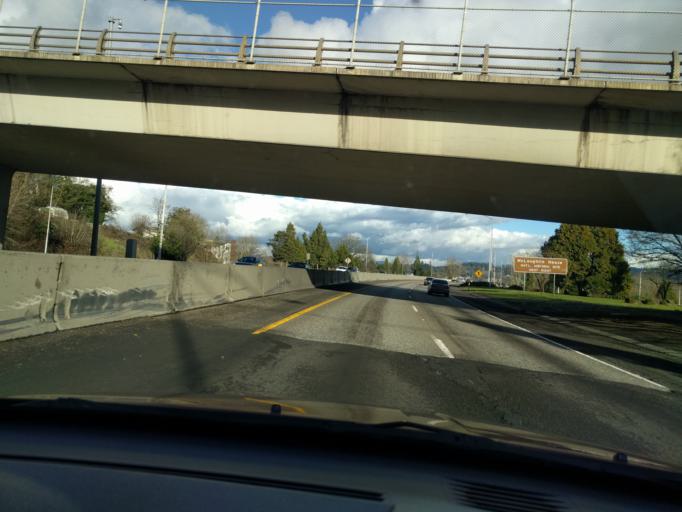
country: US
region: Oregon
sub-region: Clackamas County
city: West Linn
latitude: 45.3616
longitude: -122.6124
